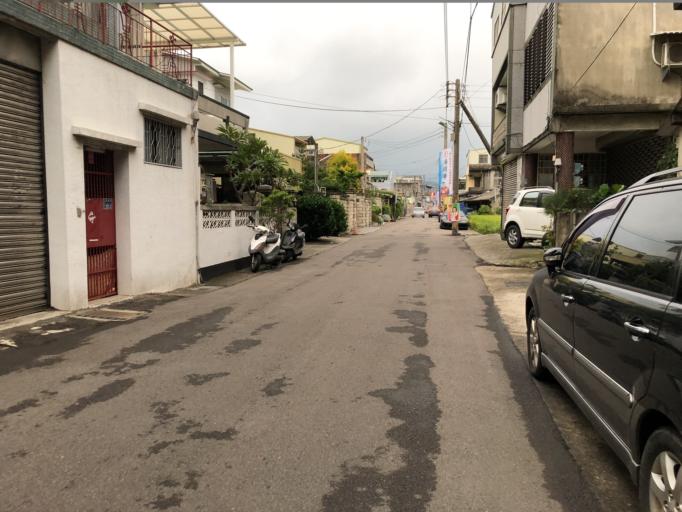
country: TW
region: Taiwan
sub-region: Miaoli
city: Miaoli
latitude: 24.5544
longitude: 120.8234
